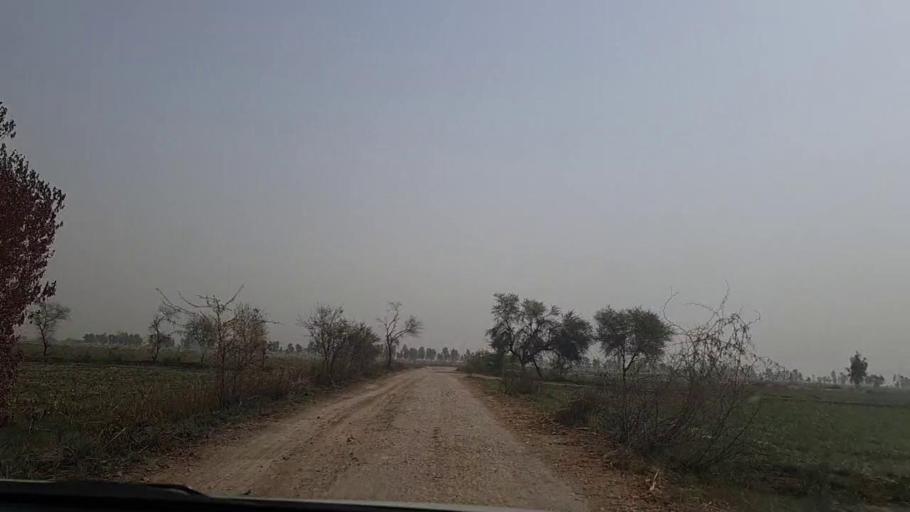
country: PK
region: Sindh
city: Pithoro
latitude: 25.4700
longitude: 69.2295
